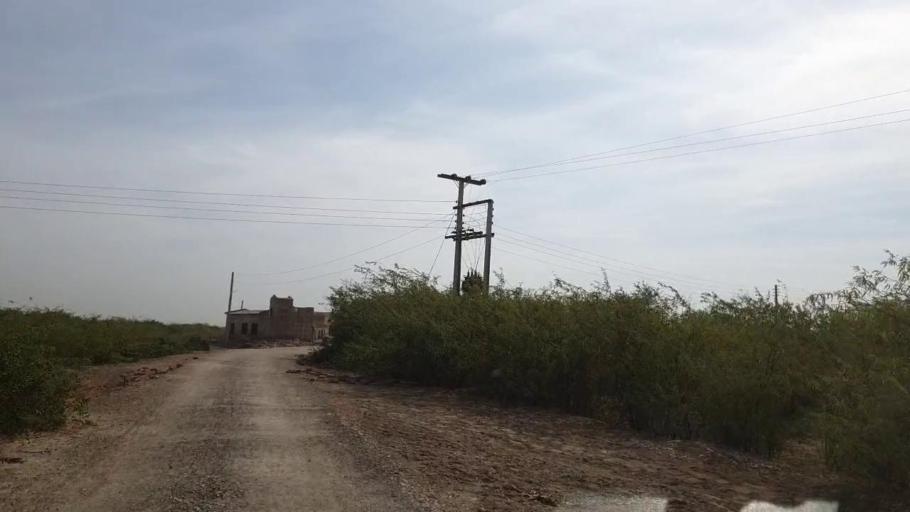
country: PK
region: Sindh
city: Kunri
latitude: 25.1826
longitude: 69.6384
